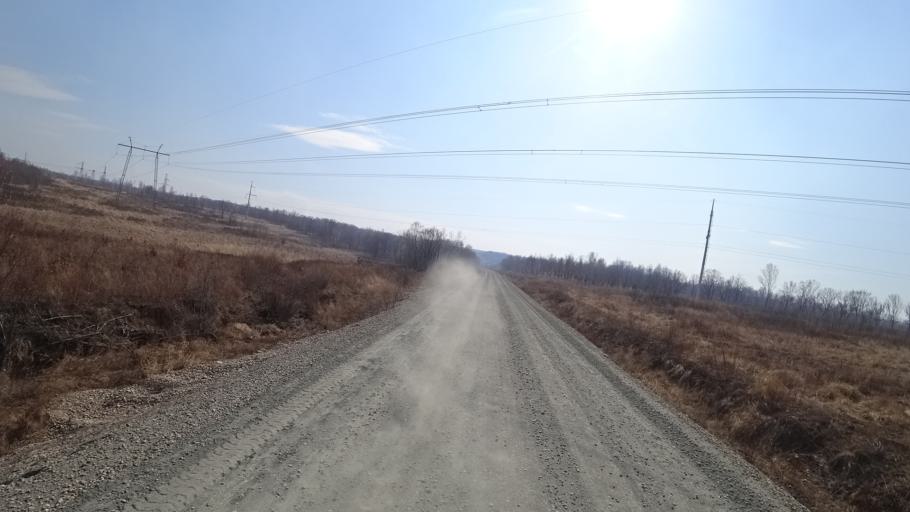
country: RU
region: Amur
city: Novobureyskiy
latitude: 49.8031
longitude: 129.9620
